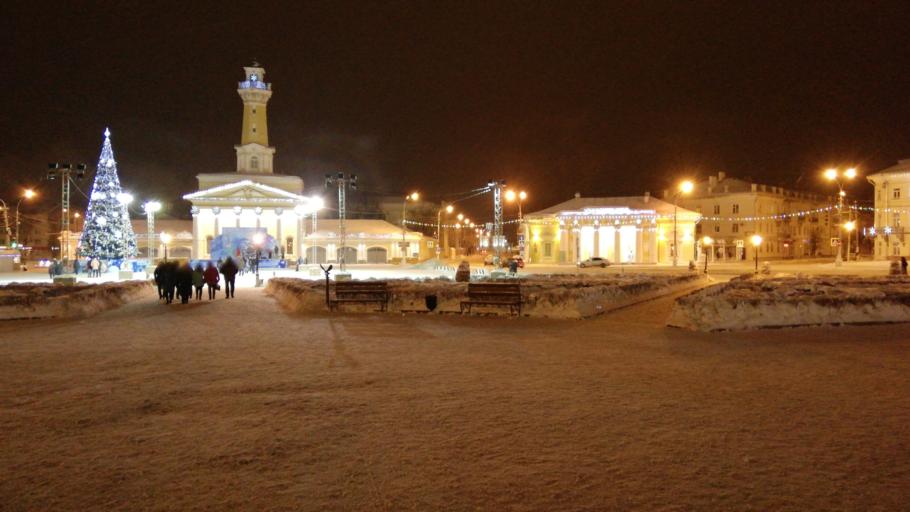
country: RU
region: Kostroma
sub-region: Kostromskoy Rayon
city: Kostroma
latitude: 57.7678
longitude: 40.9270
